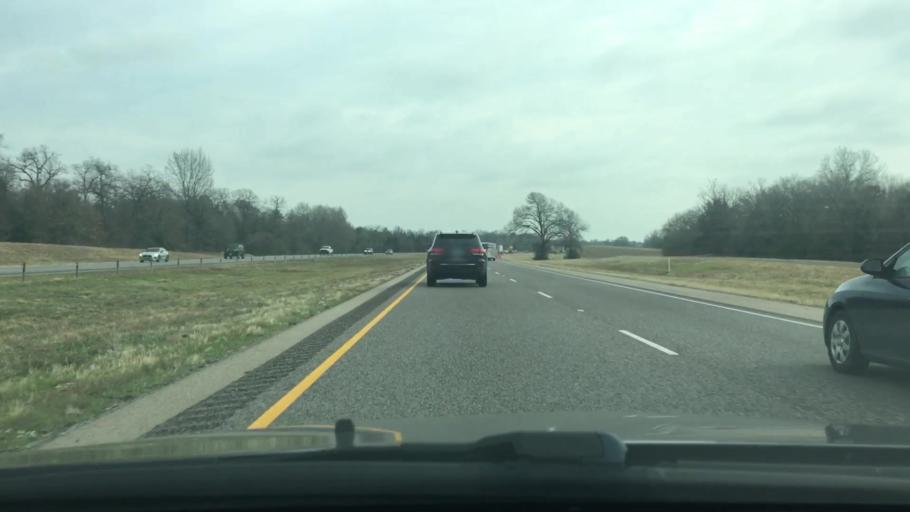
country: US
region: Texas
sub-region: Leon County
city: Buffalo
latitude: 31.5056
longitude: -96.1000
